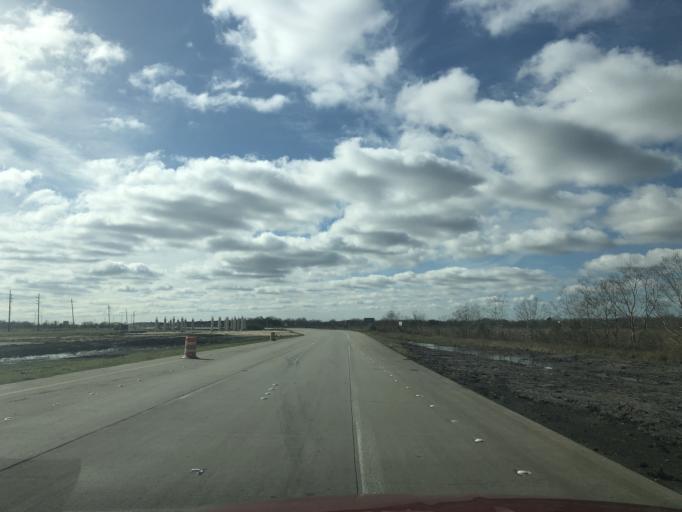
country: US
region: Texas
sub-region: Chambers County
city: Mont Belvieu
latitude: 29.8056
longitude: -94.8671
